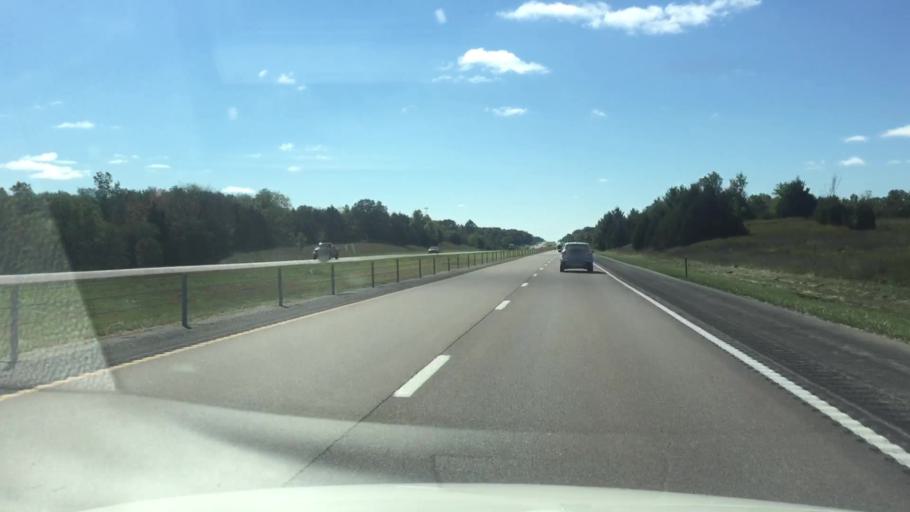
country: US
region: Missouri
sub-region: Boone County
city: Ashland
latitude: 38.7402
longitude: -92.2538
